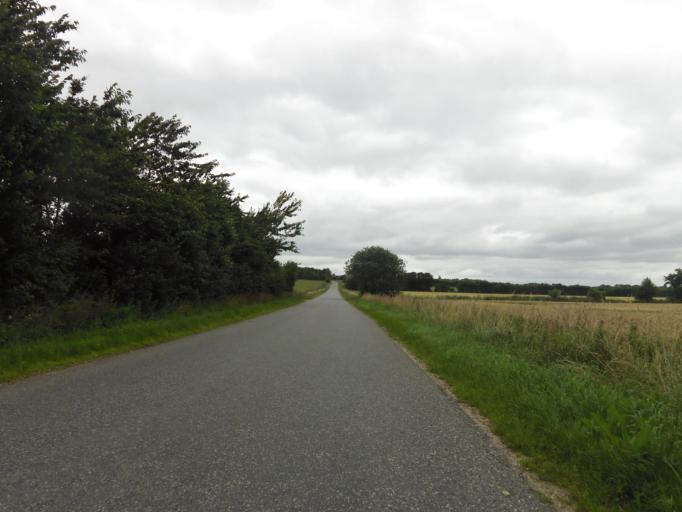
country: DK
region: South Denmark
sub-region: Haderslev Kommune
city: Gram
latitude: 55.2631
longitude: 9.1643
